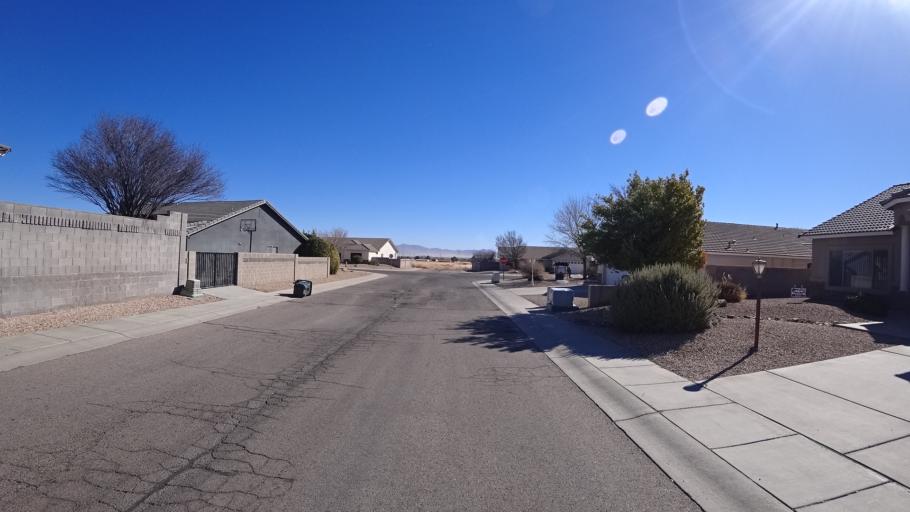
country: US
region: Arizona
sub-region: Mohave County
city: New Kingman-Butler
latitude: 35.2377
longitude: -114.0289
